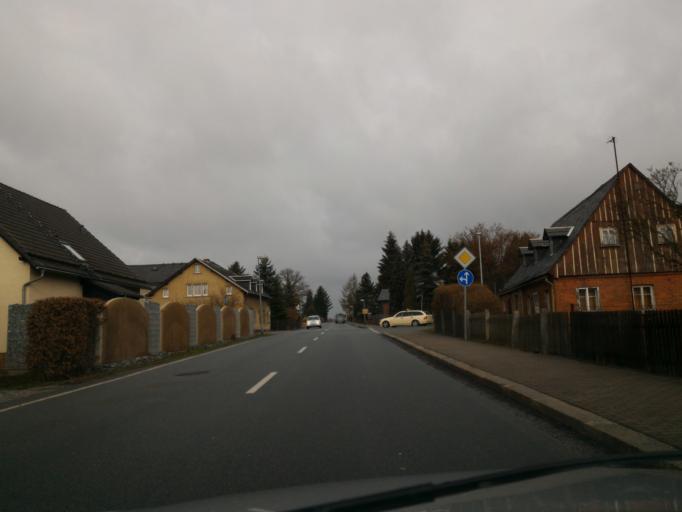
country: DE
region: Saxony
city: Eibau
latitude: 50.9715
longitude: 14.6445
